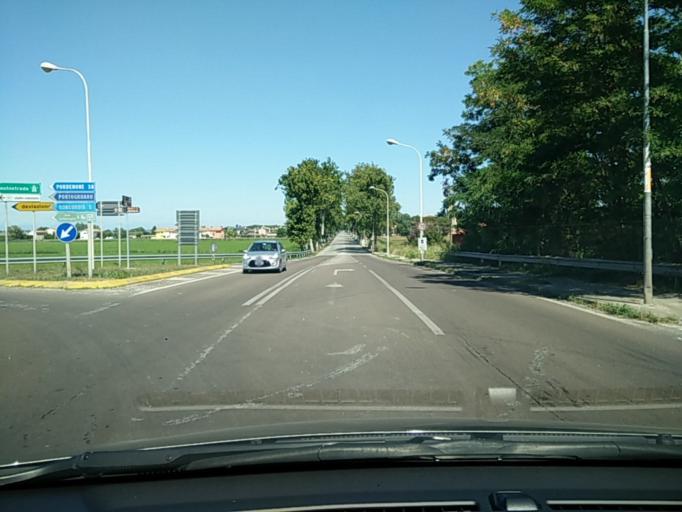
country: IT
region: Veneto
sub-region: Provincia di Venezia
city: Concordia Sagittaria
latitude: 45.7046
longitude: 12.8674
